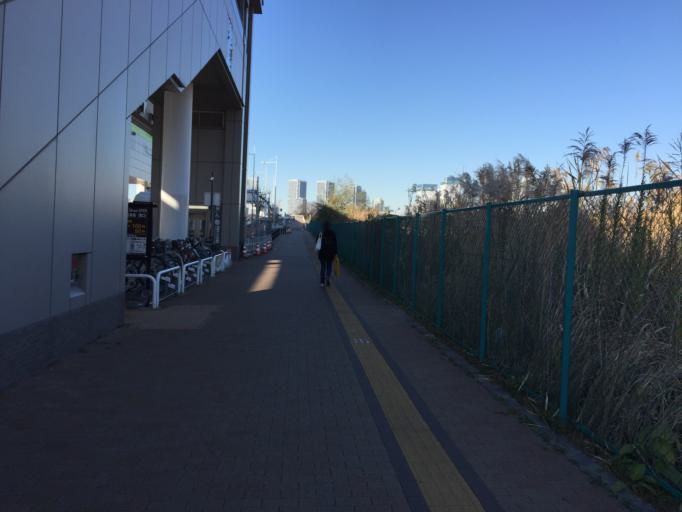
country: JP
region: Tokyo
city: Urayasu
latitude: 35.6397
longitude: 139.7895
